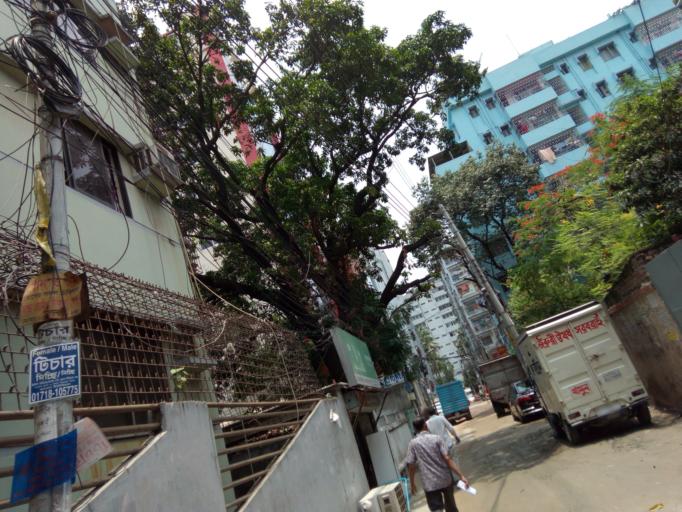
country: BD
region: Dhaka
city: Paltan
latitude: 23.7338
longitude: 90.4076
